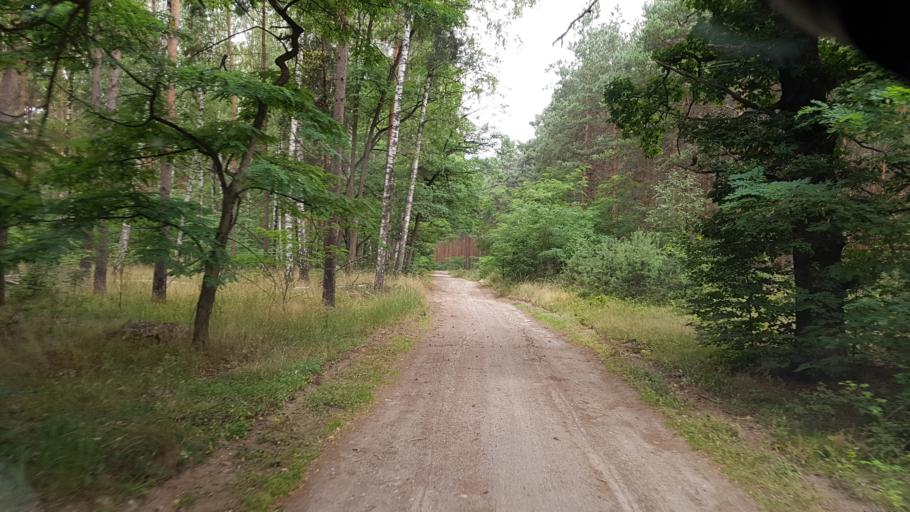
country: DE
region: Brandenburg
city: Lebusa
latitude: 51.7774
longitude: 13.3869
